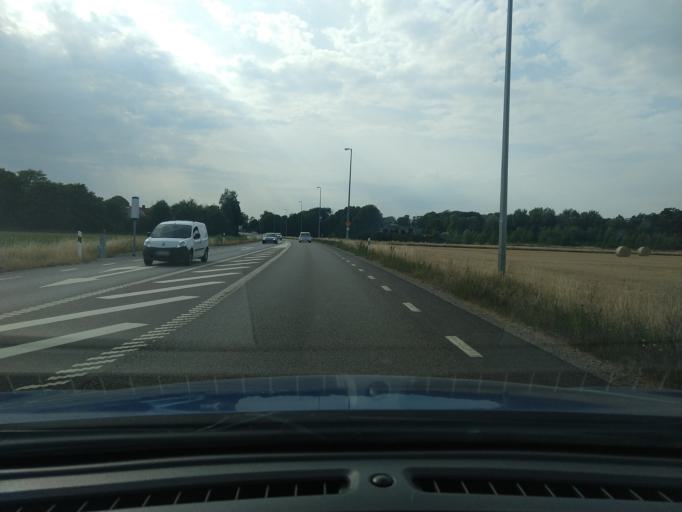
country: SE
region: Blekinge
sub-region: Karlskrona Kommun
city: Jaemjoe
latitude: 56.1851
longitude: 15.7695
